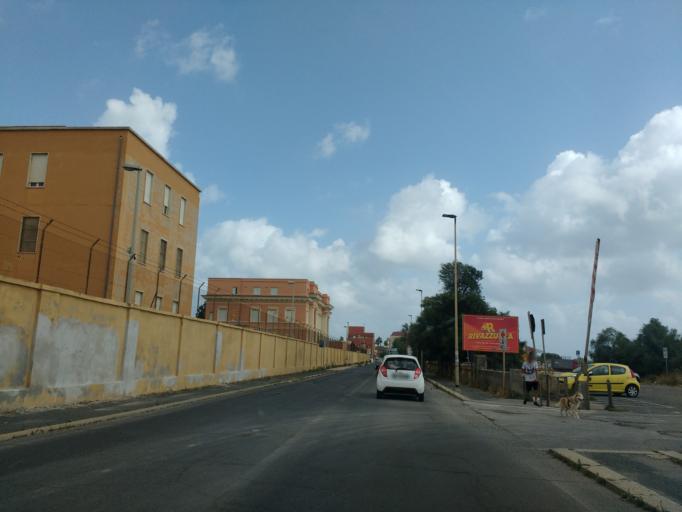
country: IT
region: Latium
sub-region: Citta metropolitana di Roma Capitale
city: Anzio
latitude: 41.4530
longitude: 12.6185
